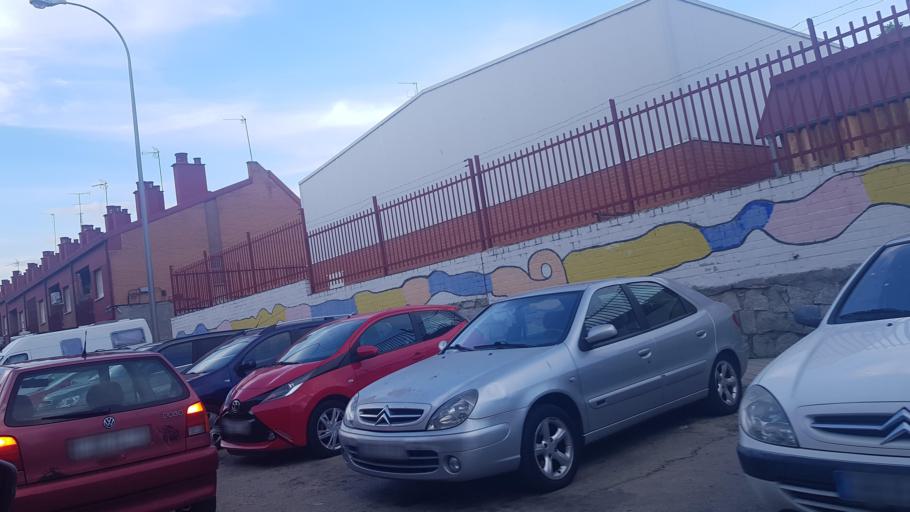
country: ES
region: Madrid
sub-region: Provincia de Madrid
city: Puente de Vallecas
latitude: 40.3710
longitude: -3.6583
